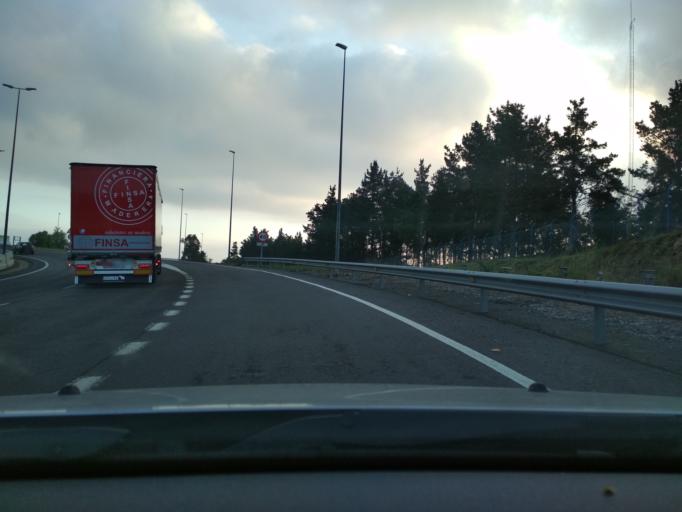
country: ES
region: Galicia
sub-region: Provincia da Coruna
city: Santiago de Compostela
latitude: 42.9066
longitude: -8.5093
